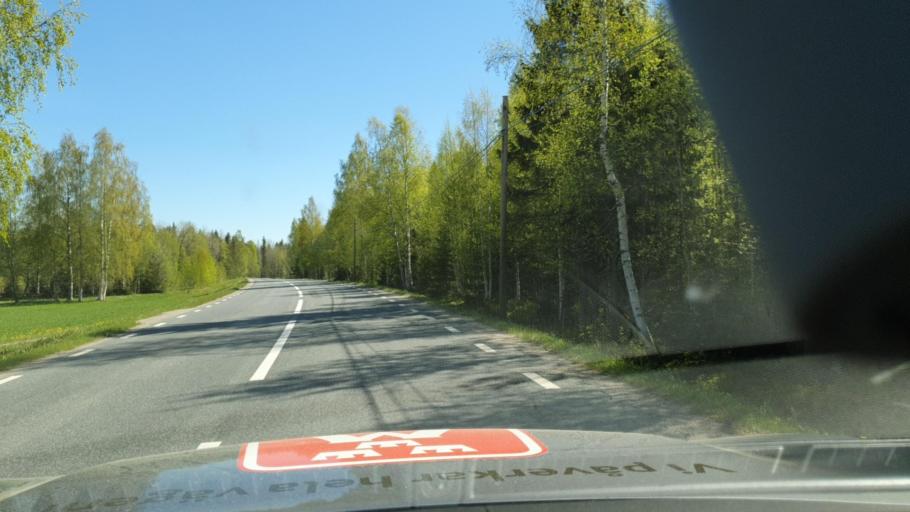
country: SE
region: Vaesternorrland
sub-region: OErnskoeldsviks Kommun
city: Ornskoldsvik
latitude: 63.6710
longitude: 18.5333
